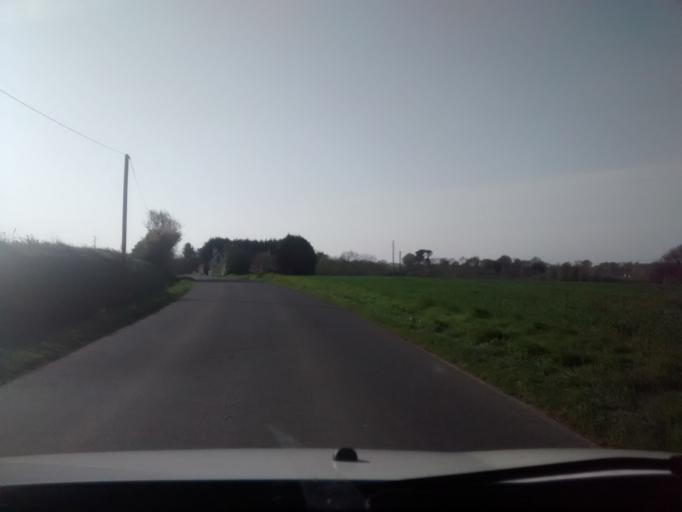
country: FR
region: Brittany
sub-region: Departement des Cotes-d'Armor
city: Trevou-Treguignec
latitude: 48.7884
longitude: -3.3345
